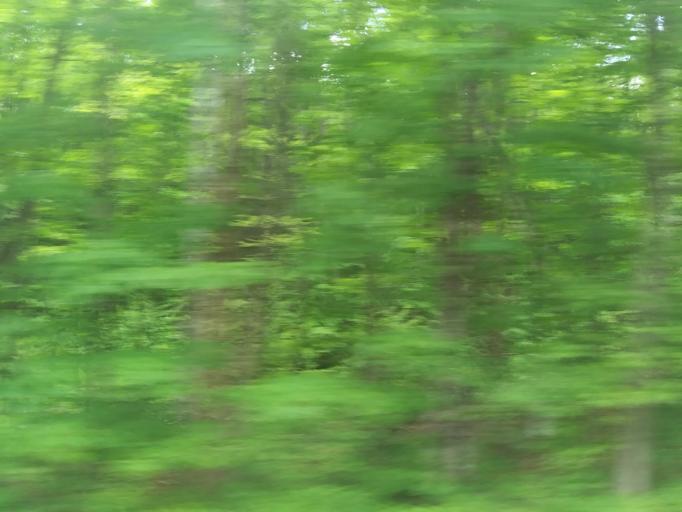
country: US
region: Massachusetts
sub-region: Franklin County
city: Buckland
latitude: 42.5827
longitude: -72.8294
